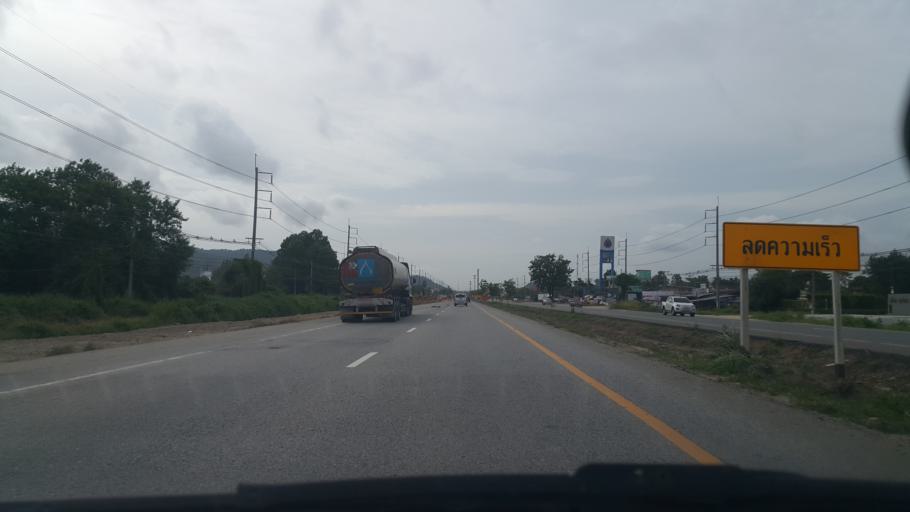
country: TH
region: Rayong
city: Nikhom Phattana
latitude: 12.8054
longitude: 101.1451
